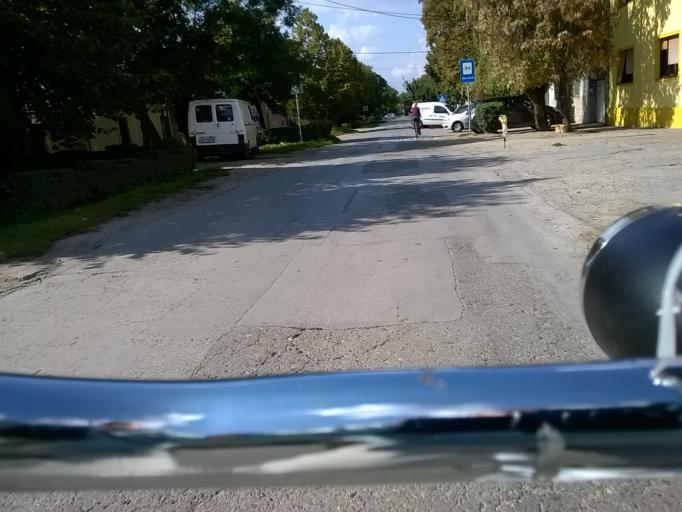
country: RS
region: Autonomna Pokrajina Vojvodina
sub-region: Juznobanatski Okrug
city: Pancevo
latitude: 44.8769
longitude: 20.6376
